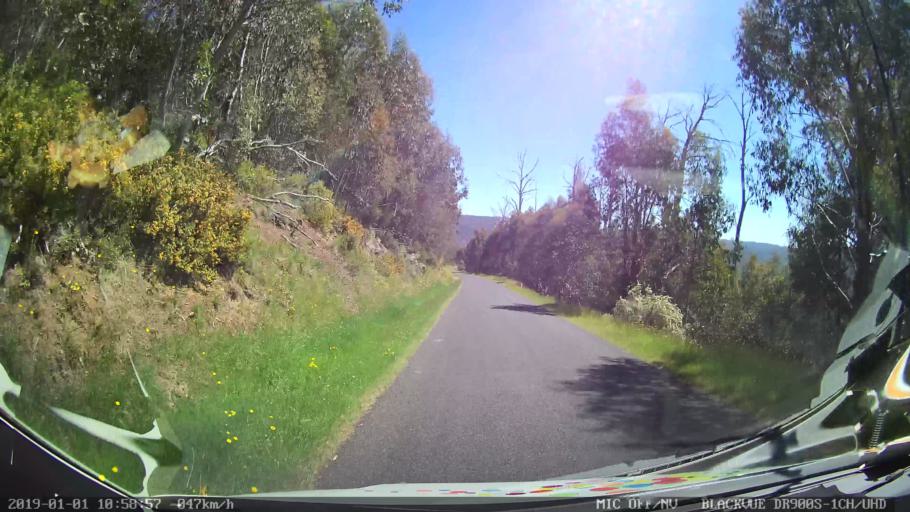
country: AU
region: New South Wales
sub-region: Snowy River
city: Jindabyne
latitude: -35.9887
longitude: 148.3985
